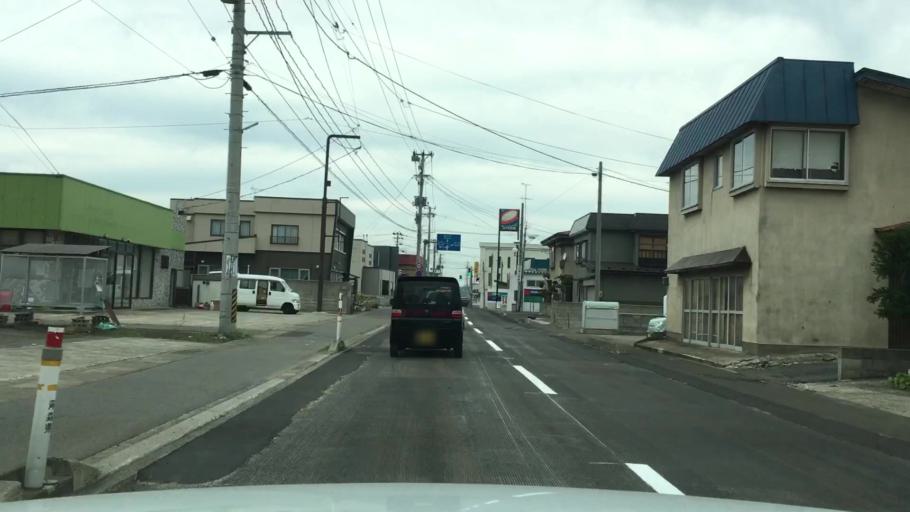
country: JP
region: Aomori
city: Hirosaki
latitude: 40.6275
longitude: 140.4544
